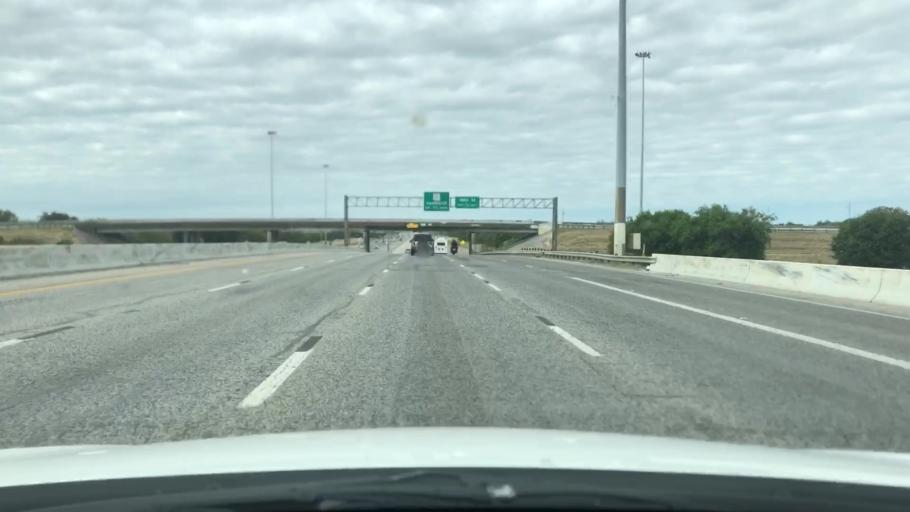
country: US
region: Texas
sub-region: Bexar County
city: Lackland Air Force Base
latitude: 29.4048
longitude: -98.5572
